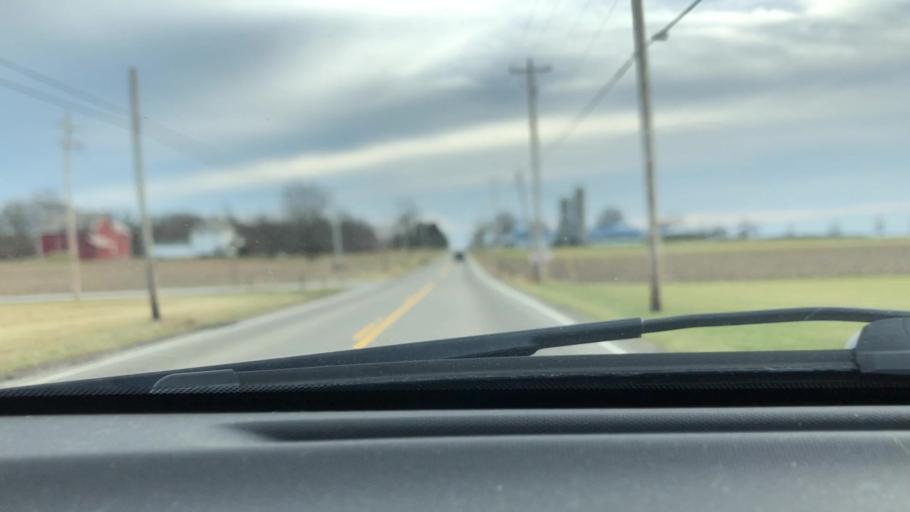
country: US
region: Ohio
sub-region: Wayne County
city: Dalton
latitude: 40.7637
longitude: -81.7453
